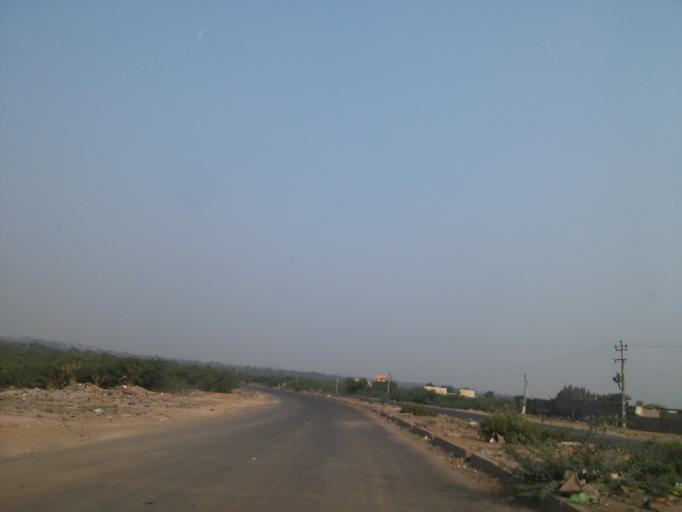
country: IN
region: Gujarat
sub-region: Kachchh
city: Bhuj
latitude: 23.2651
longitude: 69.6952
